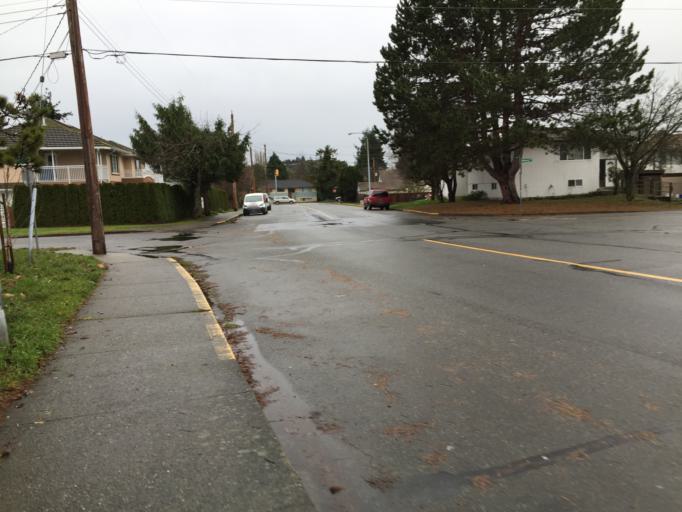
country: CA
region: British Columbia
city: Oak Bay
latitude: 48.4697
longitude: -123.3246
